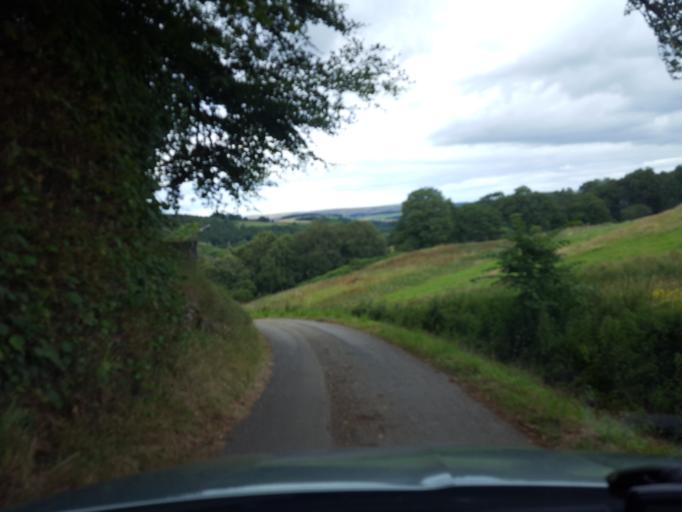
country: GB
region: Scotland
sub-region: Moray
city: Rothes
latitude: 57.4209
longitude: -3.3598
